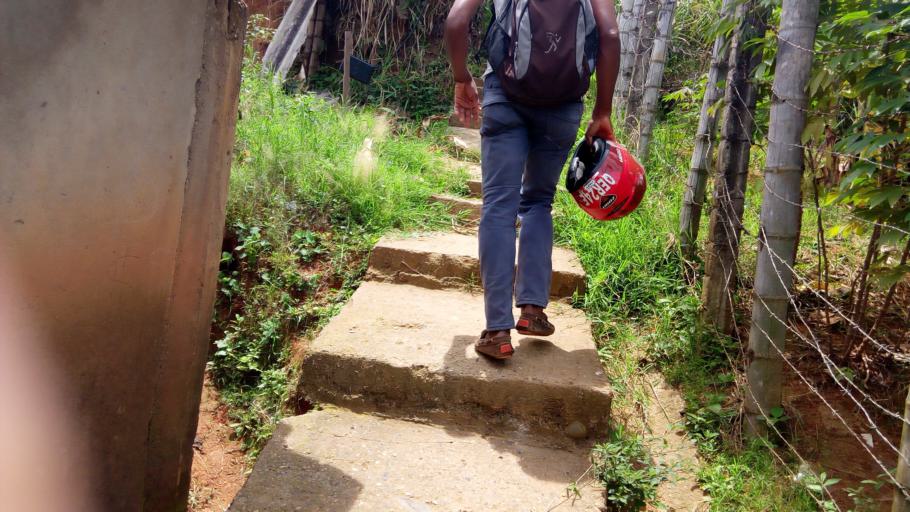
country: CO
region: Valle del Cauca
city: Cali
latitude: 3.3779
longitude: -76.5615
